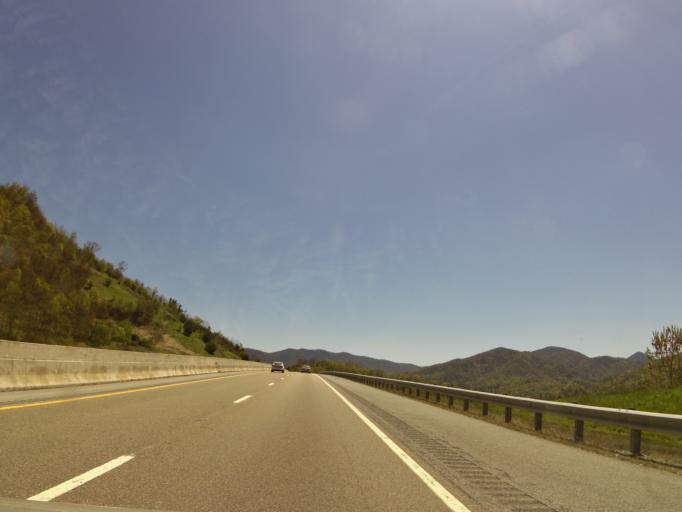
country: US
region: Tennessee
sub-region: Unicoi County
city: Banner Hill
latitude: 36.0238
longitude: -82.5451
